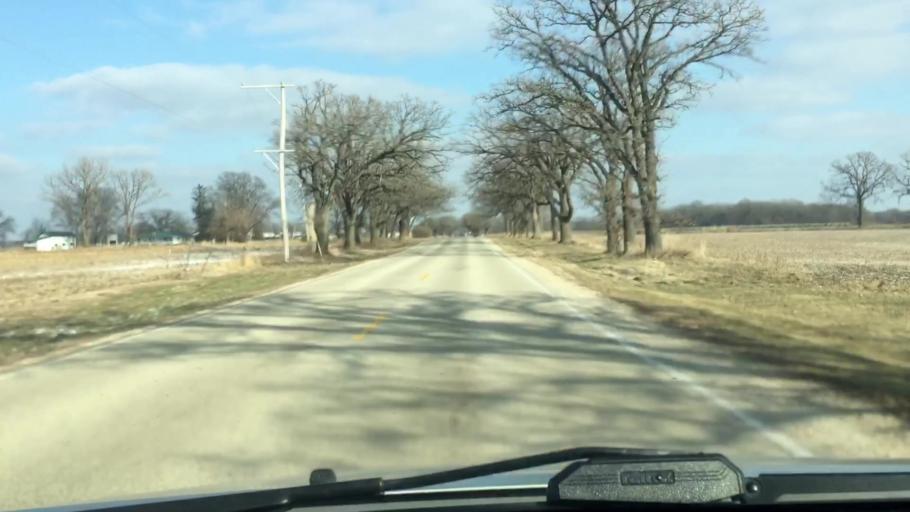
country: US
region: Wisconsin
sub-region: Waukesha County
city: Eagle
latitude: 42.9127
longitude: -88.5283
